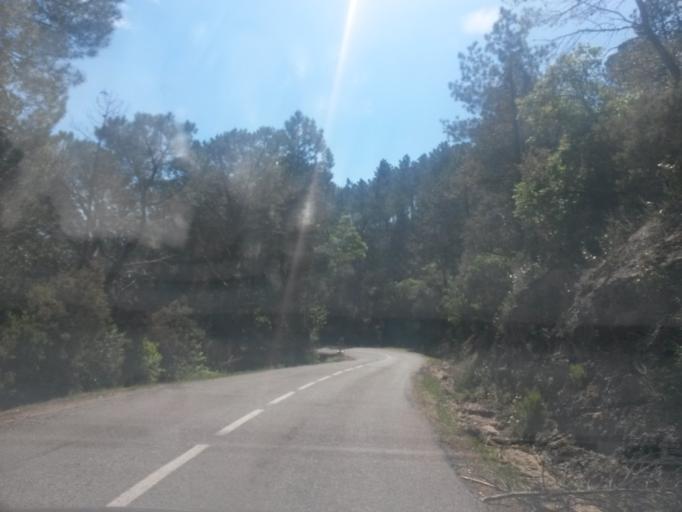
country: ES
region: Catalonia
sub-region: Provincia de Girona
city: Madremanya
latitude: 41.9831
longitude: 2.9421
